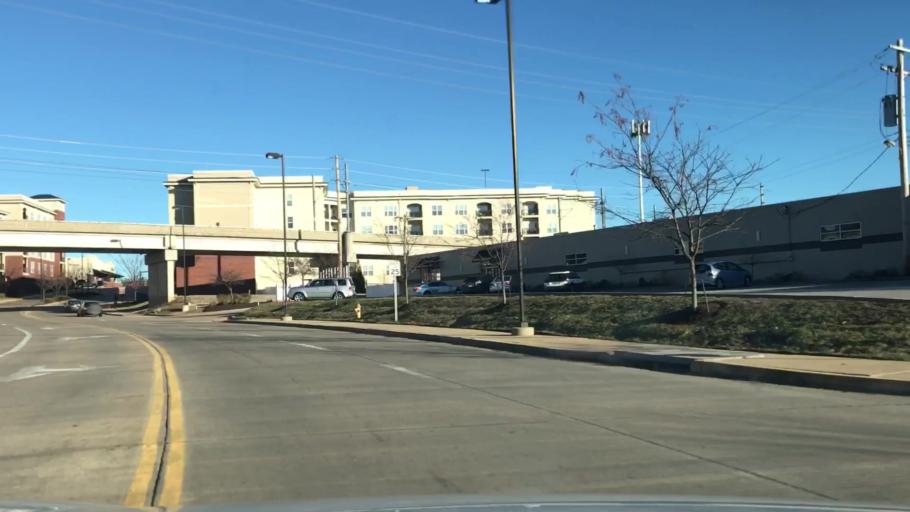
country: US
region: Missouri
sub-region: Saint Louis County
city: Brentwood
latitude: 38.6224
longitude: -90.3376
